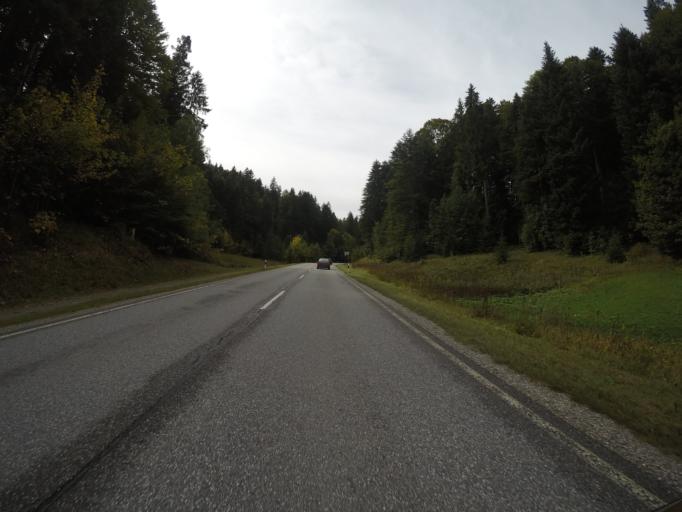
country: AT
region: Tyrol
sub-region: Politischer Bezirk Schwaz
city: Achenkirch
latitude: 47.6073
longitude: 11.6389
